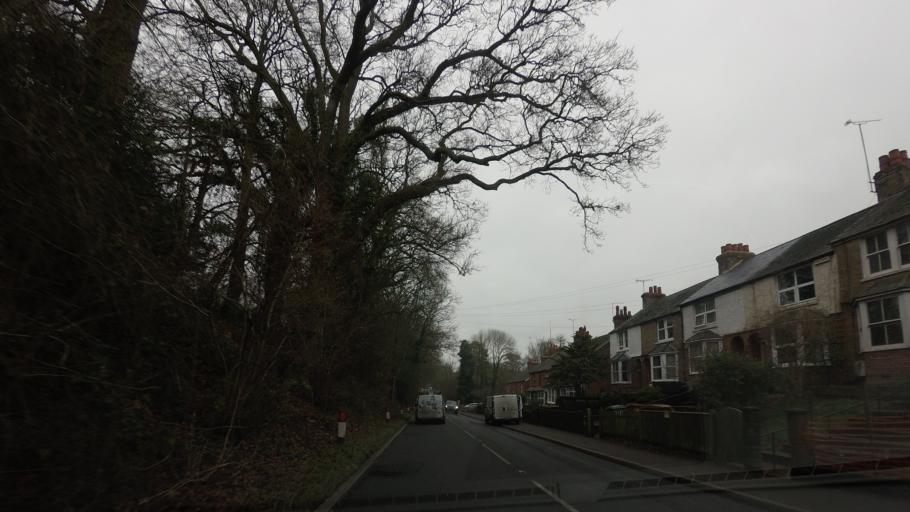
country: GB
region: England
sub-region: Kent
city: Hawkhurst
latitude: 51.0535
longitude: 0.5077
